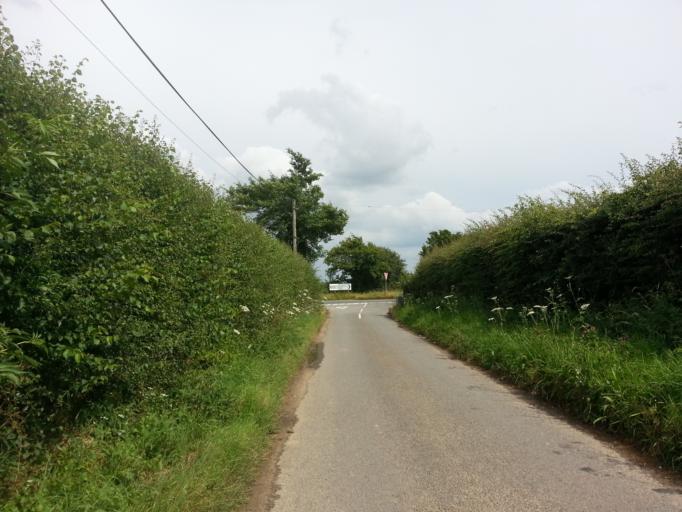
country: GB
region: England
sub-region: Suffolk
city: Ipswich
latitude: 52.0065
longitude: 1.1647
